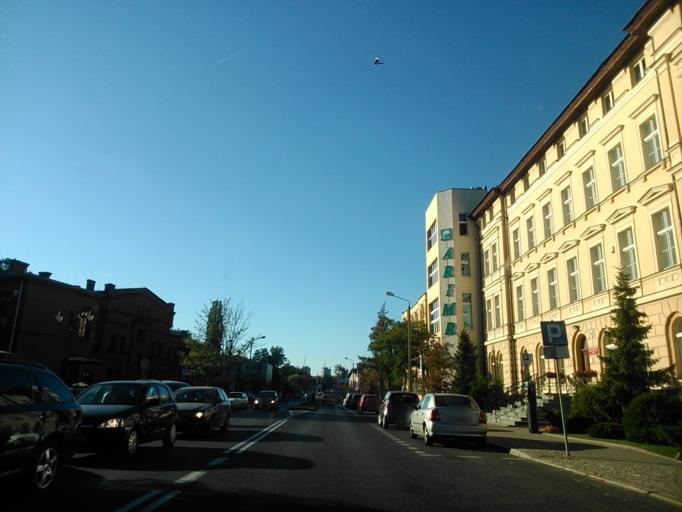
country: PL
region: Kujawsko-Pomorskie
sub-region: Torun
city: Torun
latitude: 53.0140
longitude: 18.6126
